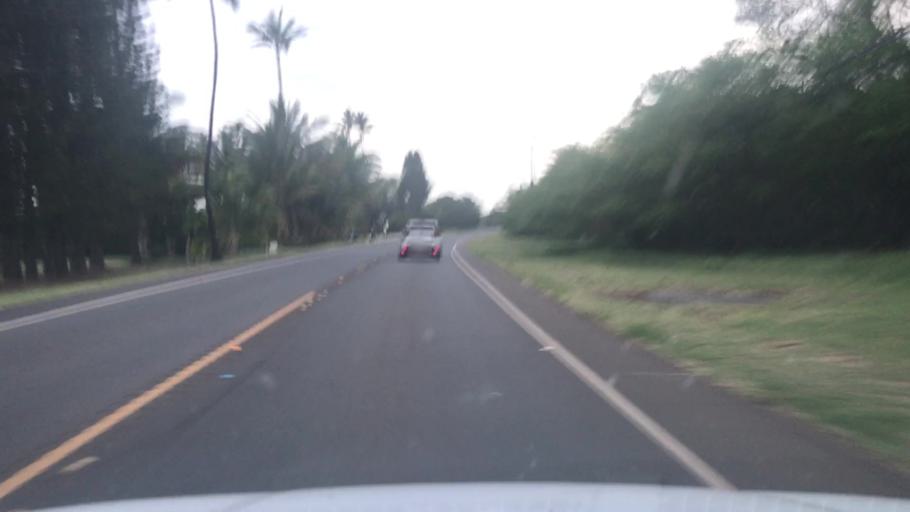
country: US
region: Hawaii
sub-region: Maui County
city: Kaunakakai
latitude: 21.0672
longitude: -156.9567
